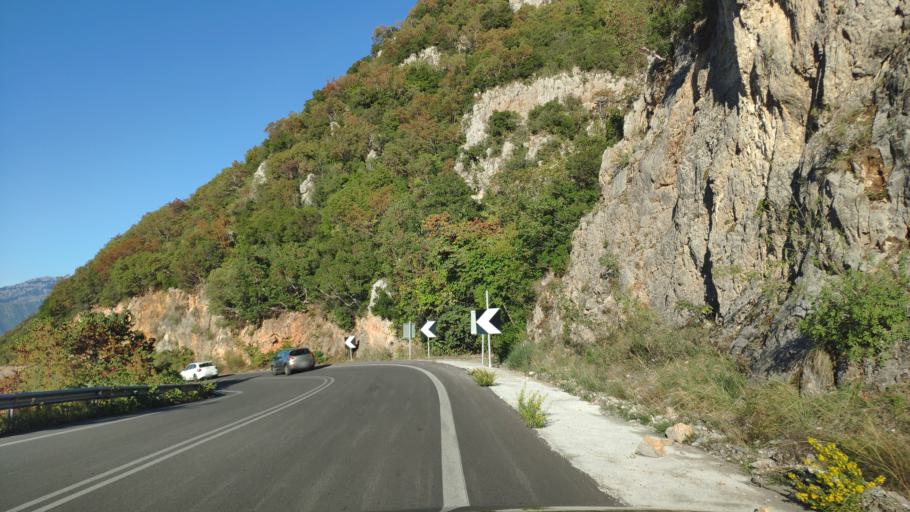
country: GR
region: Peloponnese
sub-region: Nomos Arkadias
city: Langadhia
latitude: 37.7173
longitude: 22.2006
